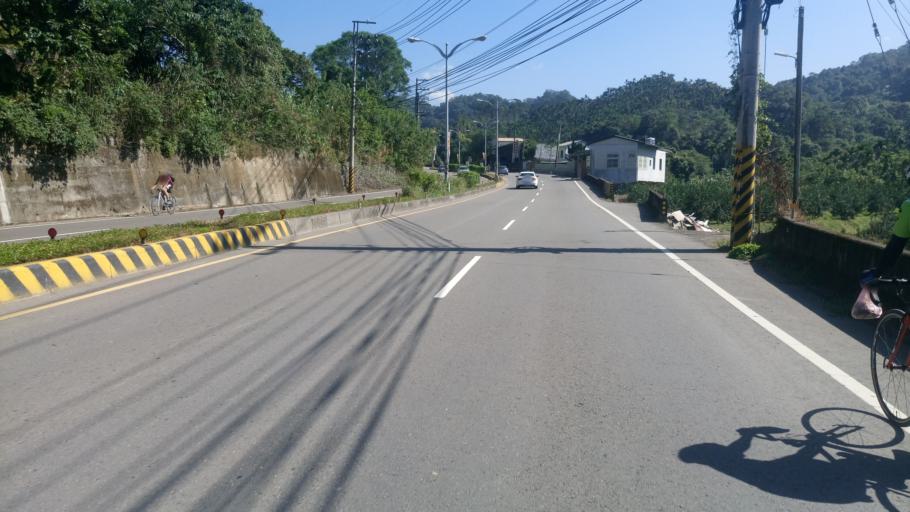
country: TW
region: Taiwan
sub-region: Hsinchu
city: Zhubei
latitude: 24.7175
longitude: 121.1486
